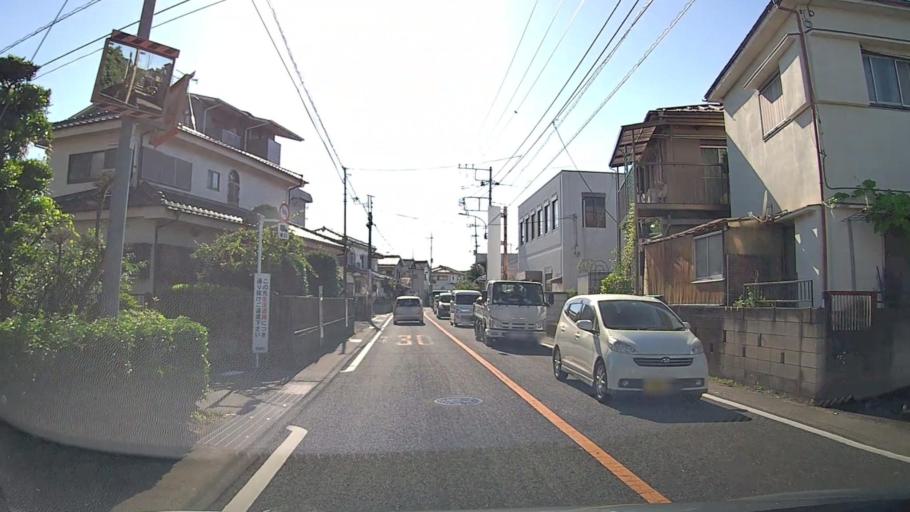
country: JP
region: Tokyo
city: Fussa
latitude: 35.7664
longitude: 139.3603
